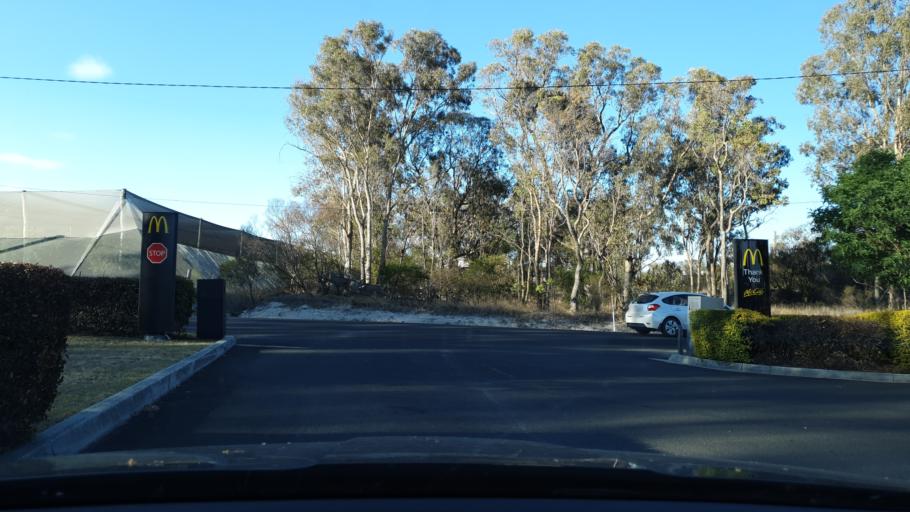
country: AU
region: Queensland
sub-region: Southern Downs
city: Stanthorpe
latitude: -28.6304
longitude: 151.9538
